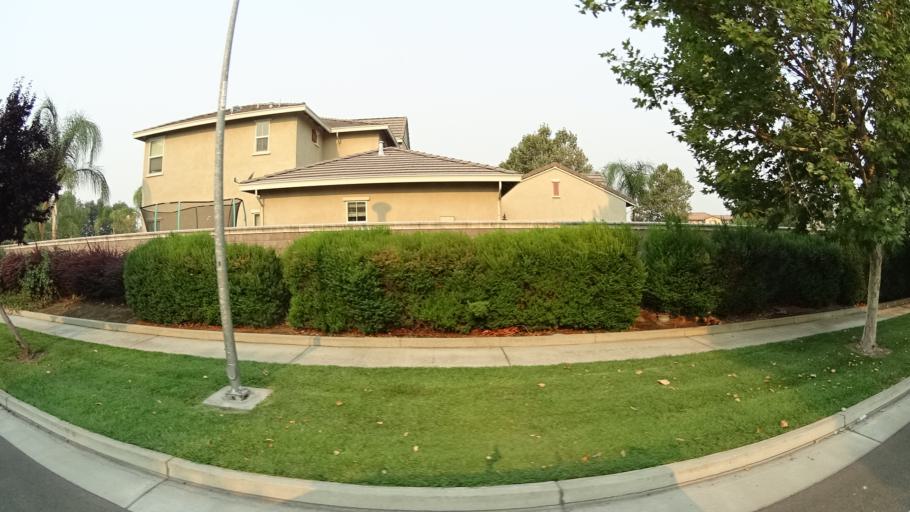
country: US
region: California
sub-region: Sacramento County
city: Laguna
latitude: 38.4057
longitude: -121.4409
